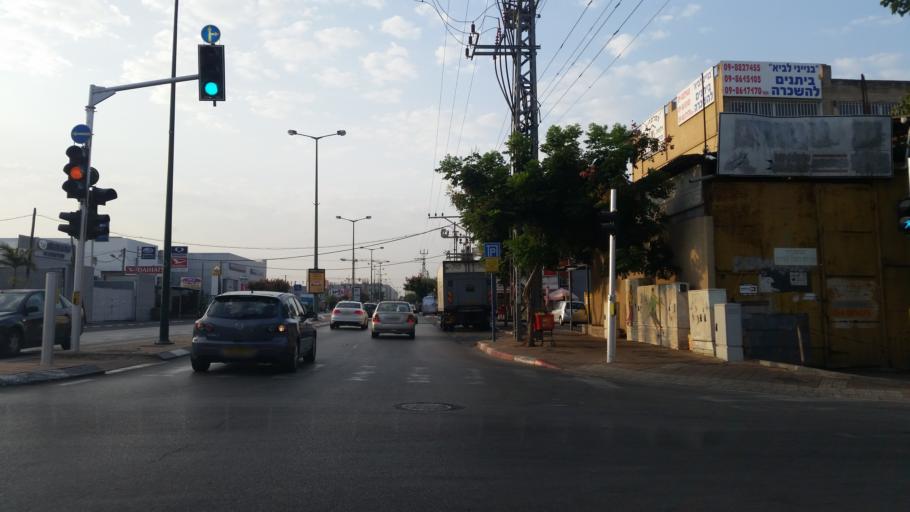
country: IL
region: Central District
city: Bet Yizhaq
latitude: 32.3202
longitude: 34.8742
